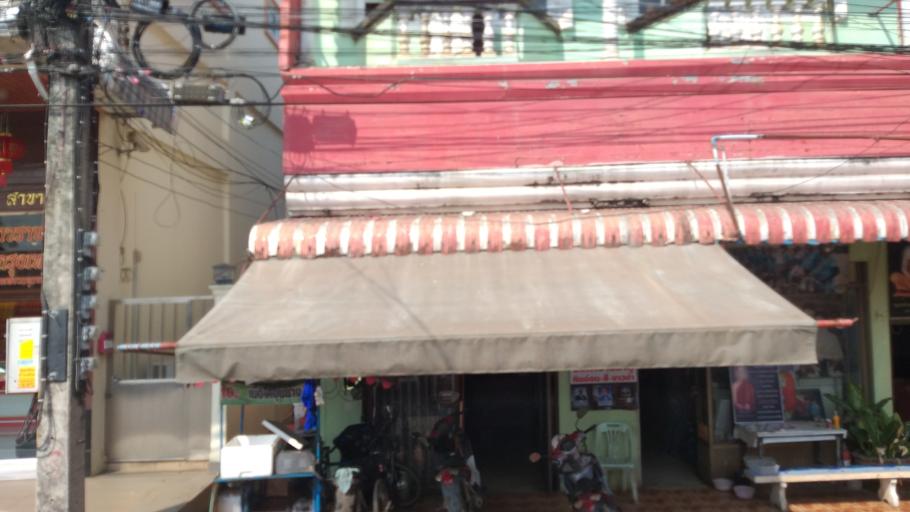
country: TH
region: Changwat Udon Thani
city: Nong Han
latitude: 17.3630
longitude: 103.1037
